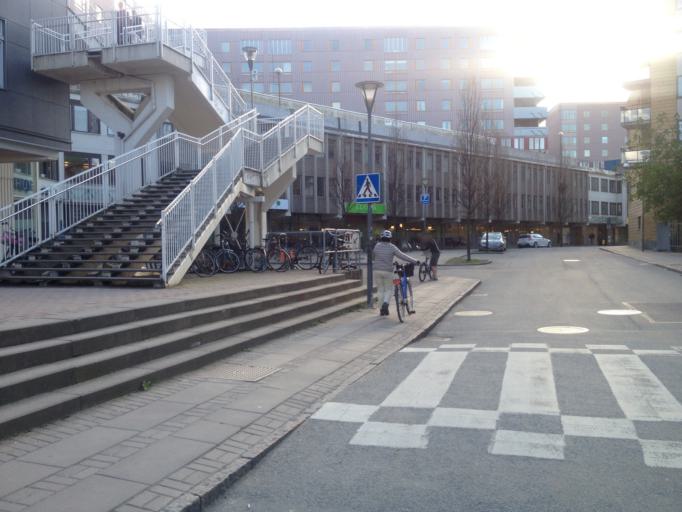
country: SE
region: Vaestra Goetaland
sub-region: Goteborg
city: Goeteborg
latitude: 57.6986
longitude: 11.9429
